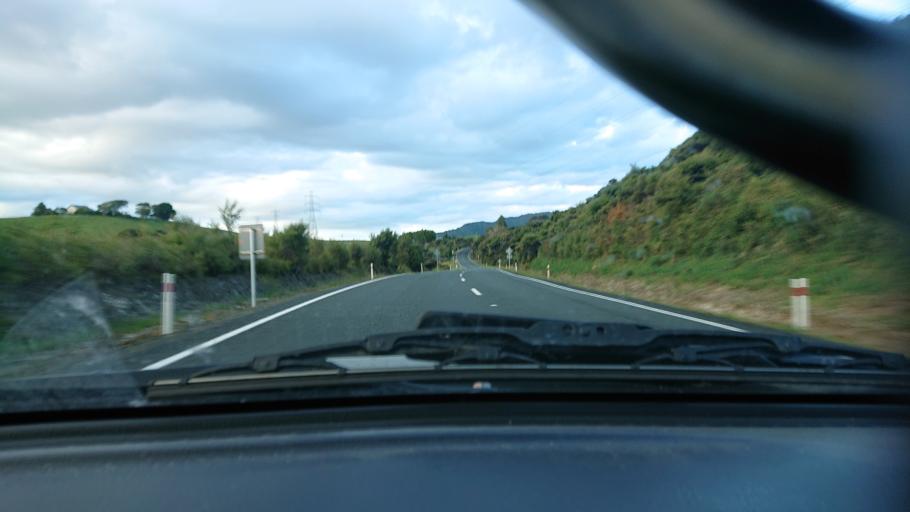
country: NZ
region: Auckland
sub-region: Auckland
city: Parakai
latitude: -36.4792
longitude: 174.4475
